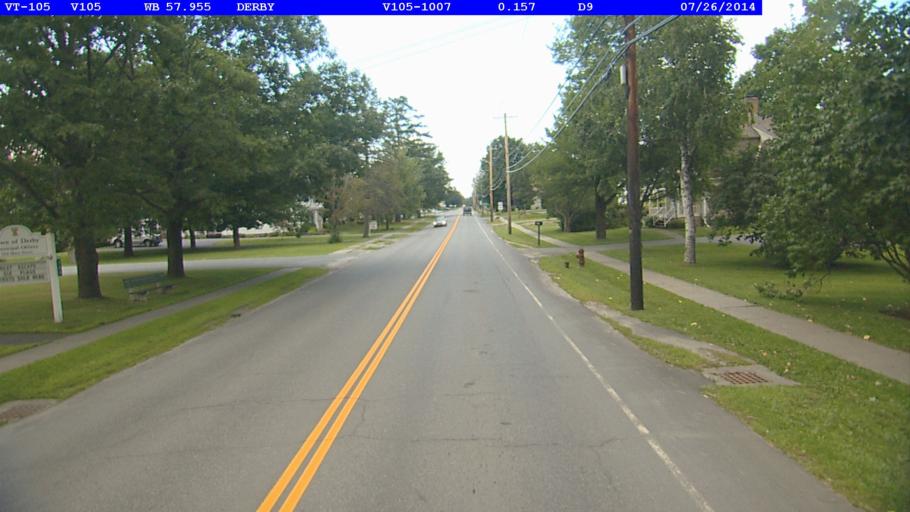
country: US
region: Vermont
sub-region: Orleans County
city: Newport
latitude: 44.9524
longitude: -72.1313
